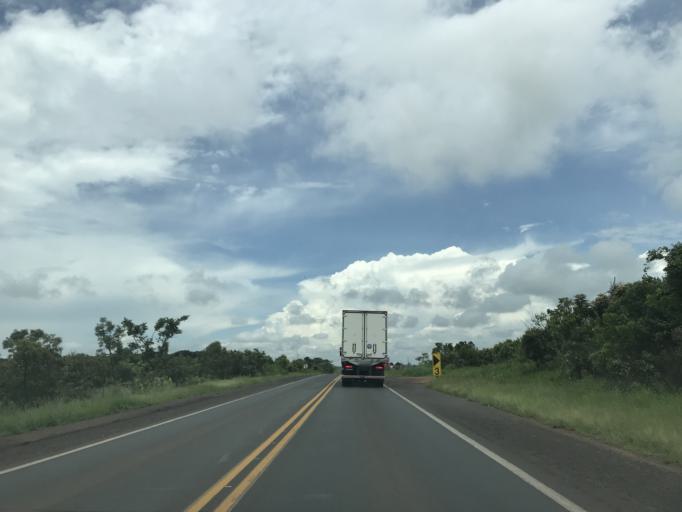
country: BR
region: Minas Gerais
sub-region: Frutal
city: Frutal
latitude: -19.7336
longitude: -48.9727
